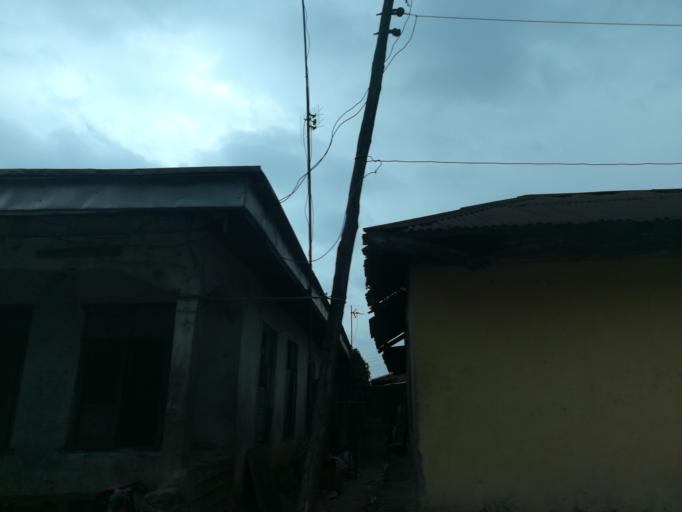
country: NG
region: Rivers
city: Port Harcourt
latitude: 4.7950
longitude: 6.9869
